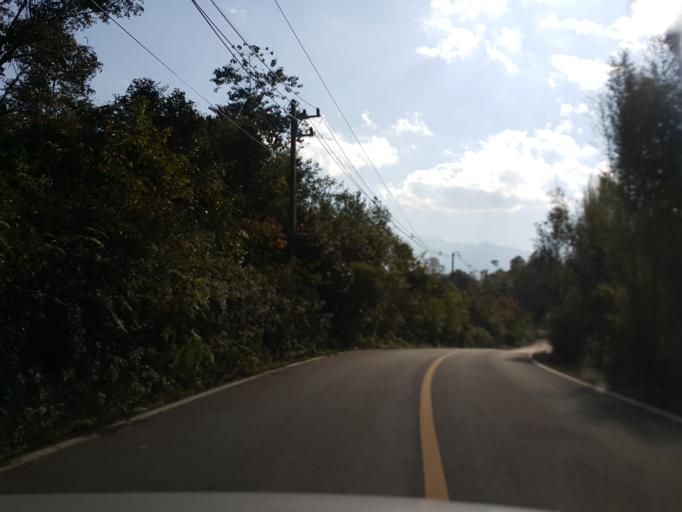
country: TH
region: Chiang Mai
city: Mae Wang
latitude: 18.6734
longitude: 98.5533
